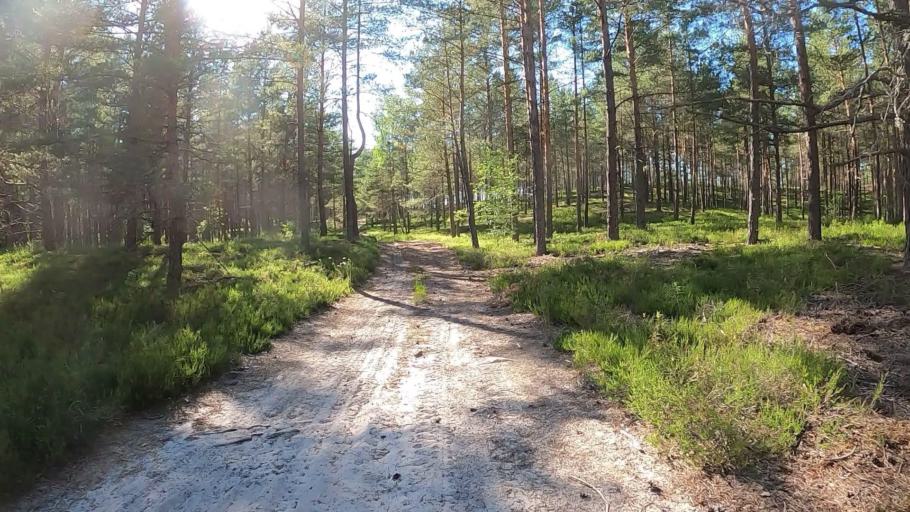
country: LV
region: Carnikava
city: Carnikava
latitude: 57.0915
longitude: 24.2526
